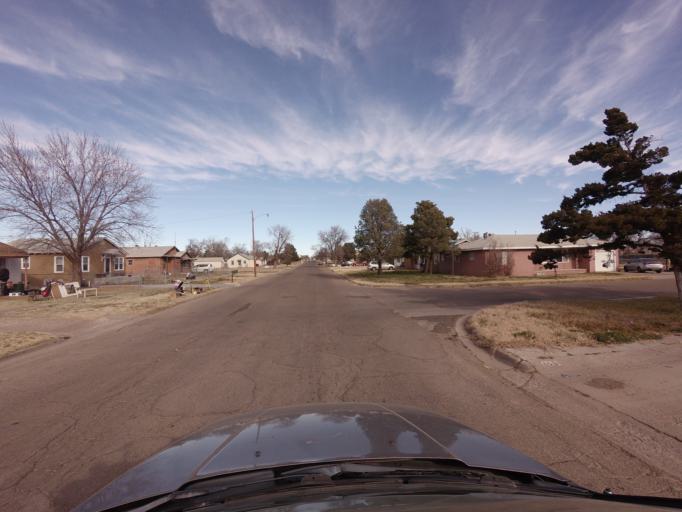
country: US
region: New Mexico
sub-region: Curry County
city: Clovis
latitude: 34.4143
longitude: -103.1990
